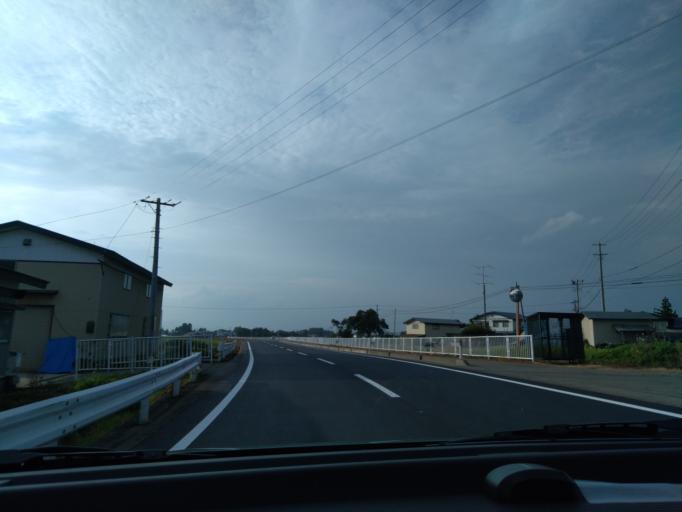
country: JP
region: Akita
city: Yokotemachi
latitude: 39.3778
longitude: 140.5338
